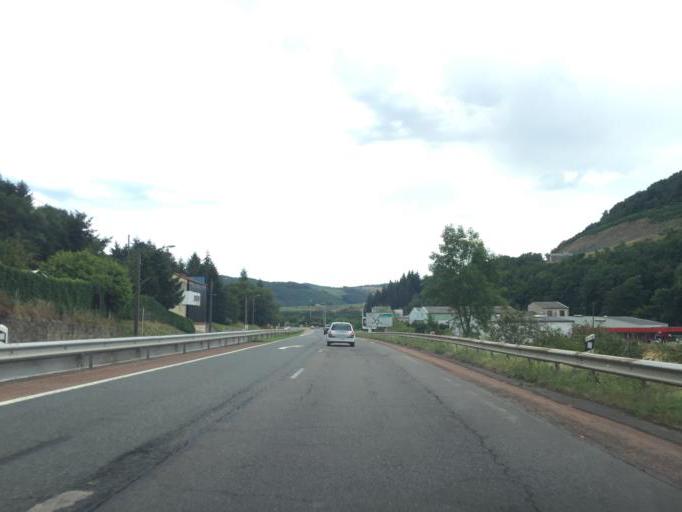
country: FR
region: Rhone-Alpes
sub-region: Departement du Rhone
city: Pontcharra-sur-Turdine
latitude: 45.8819
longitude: 4.4721
